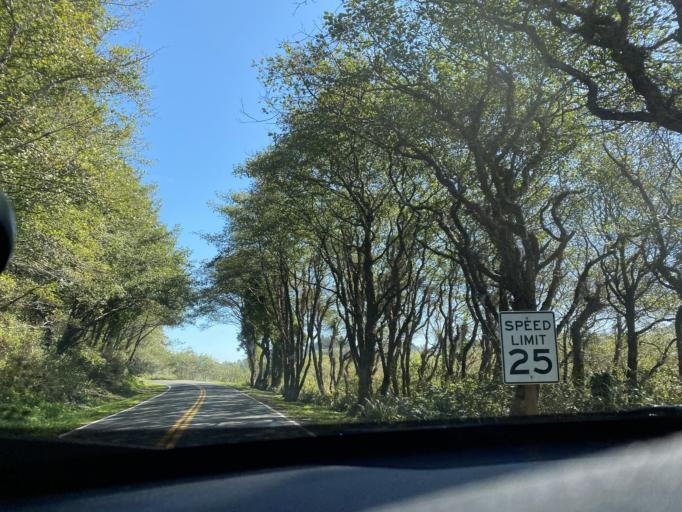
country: US
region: Washington
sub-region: Clallam County
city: Forks
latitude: 47.9205
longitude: -124.6369
